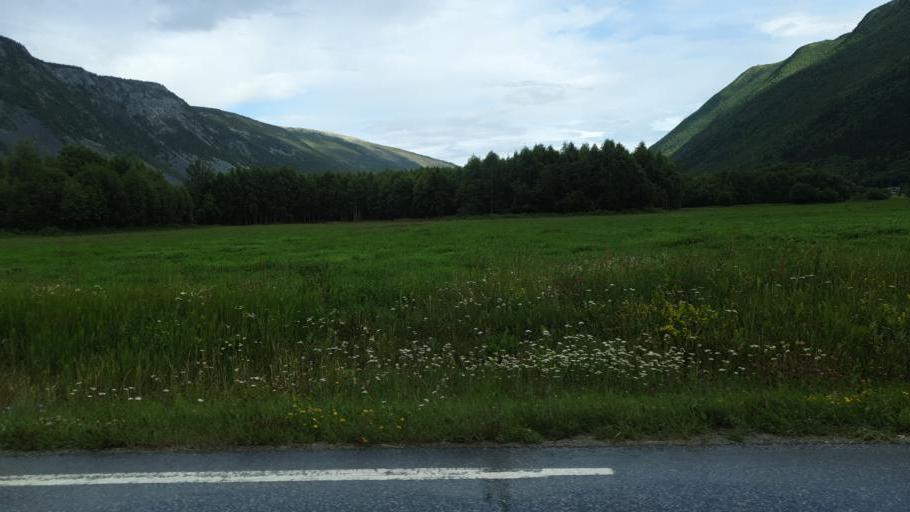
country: NO
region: Oppland
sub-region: Sel
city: Otta
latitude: 61.8430
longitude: 9.4128
